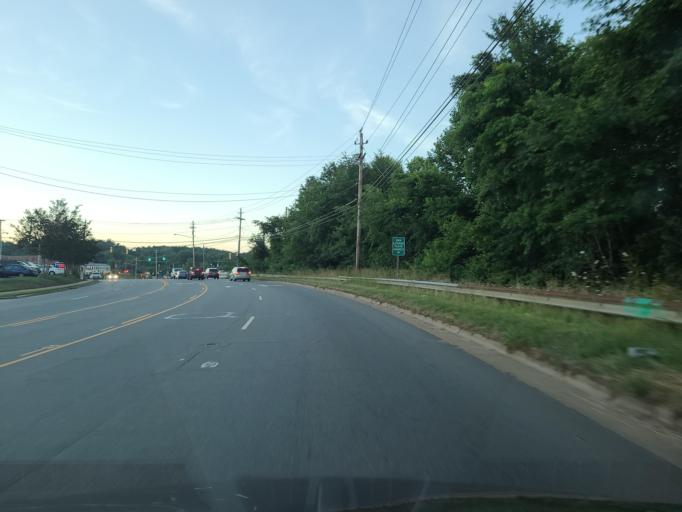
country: US
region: North Carolina
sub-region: Burke County
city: Morganton
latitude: 35.7370
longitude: -81.6795
